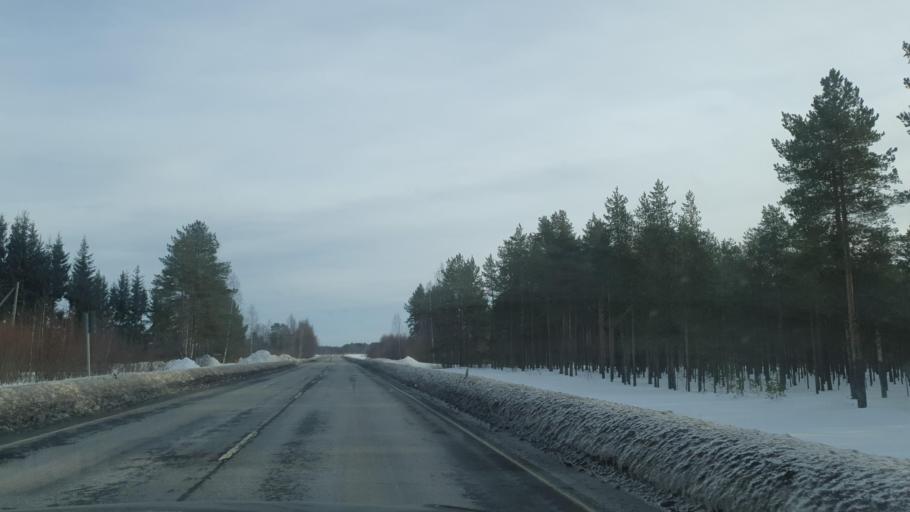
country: FI
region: Northern Ostrobothnia
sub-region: Oulunkaari
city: Utajaervi
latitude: 64.7267
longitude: 26.4903
